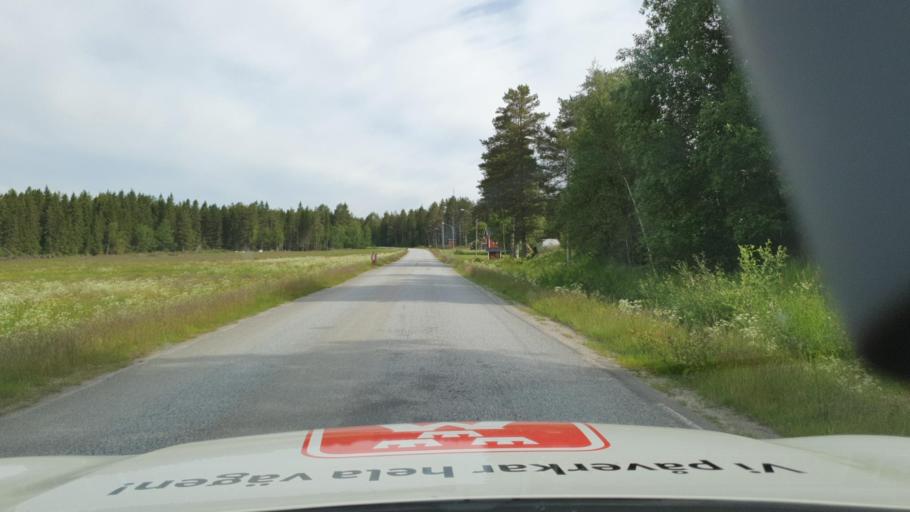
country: SE
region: Vaesterbotten
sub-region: Umea Kommun
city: Saevar
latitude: 63.9002
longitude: 20.7663
